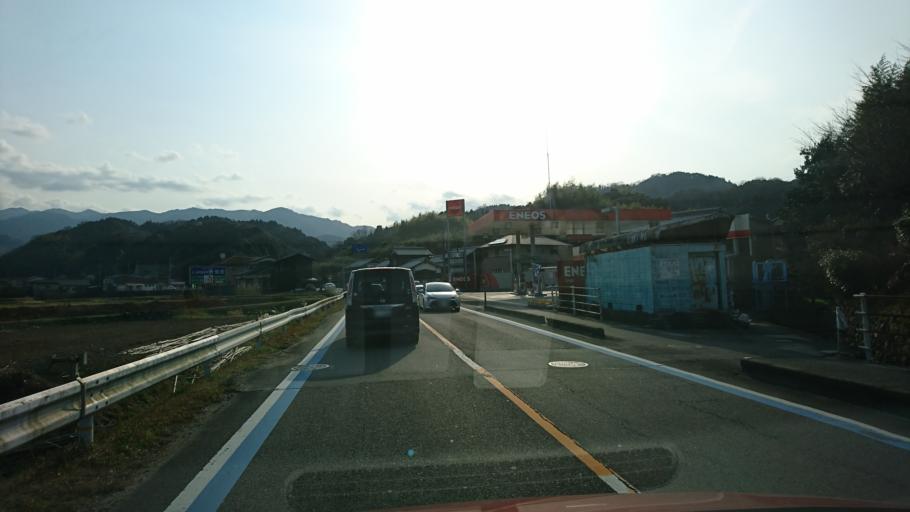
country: JP
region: Ehime
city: Hojo
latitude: 34.0042
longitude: 132.9385
